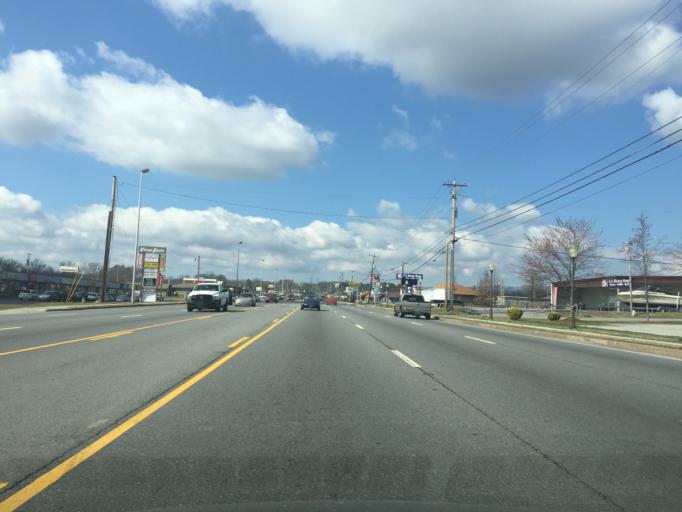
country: US
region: Georgia
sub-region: Catoosa County
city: Fort Oglethorpe
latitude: 34.9529
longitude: -85.2463
